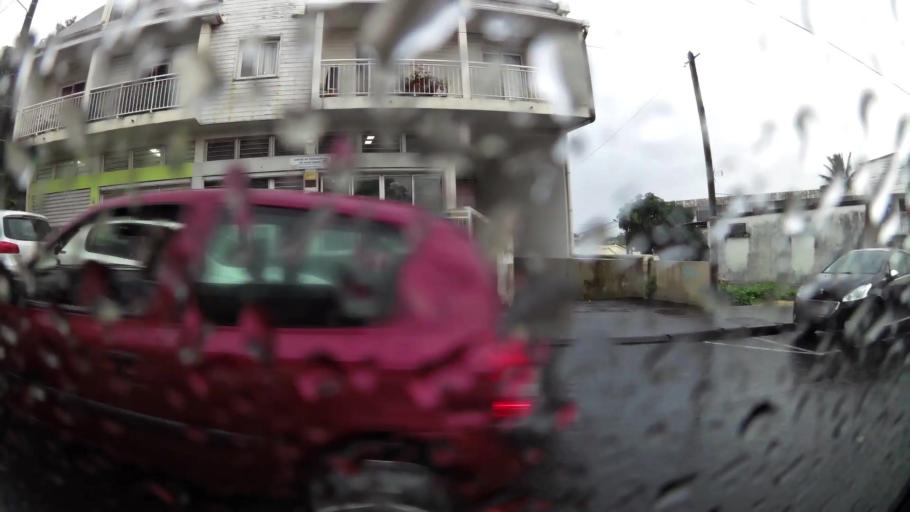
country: RE
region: Reunion
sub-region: Reunion
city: Saint-Benoit
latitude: -21.0322
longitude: 55.7118
